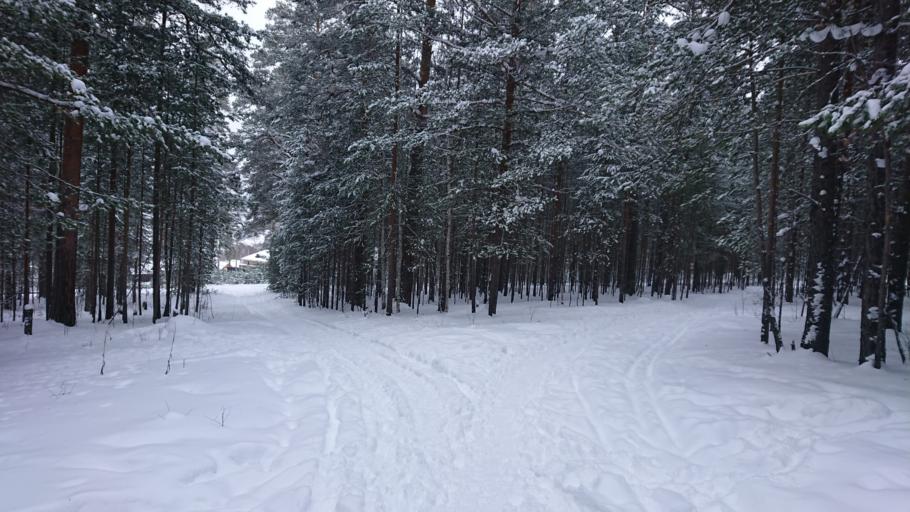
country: RU
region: Sverdlovsk
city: Degtyarsk
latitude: 56.6953
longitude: 60.0656
